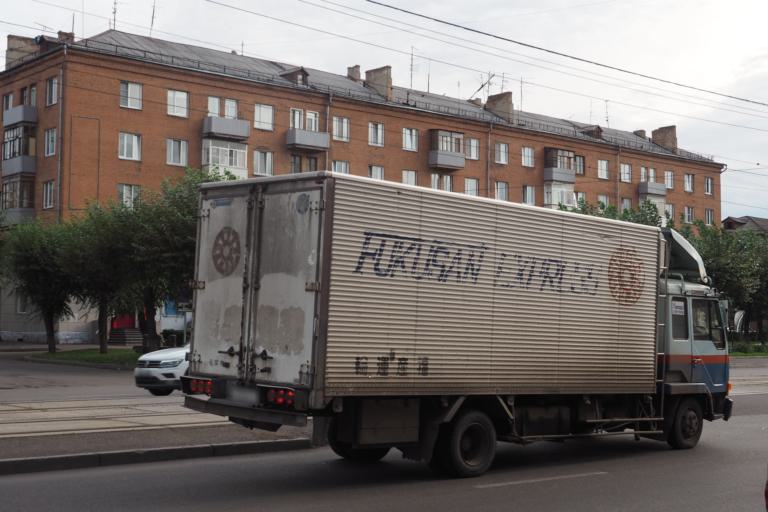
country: RU
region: Krasnoyarskiy
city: Krasnoyarsk
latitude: 56.0046
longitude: 92.9387
